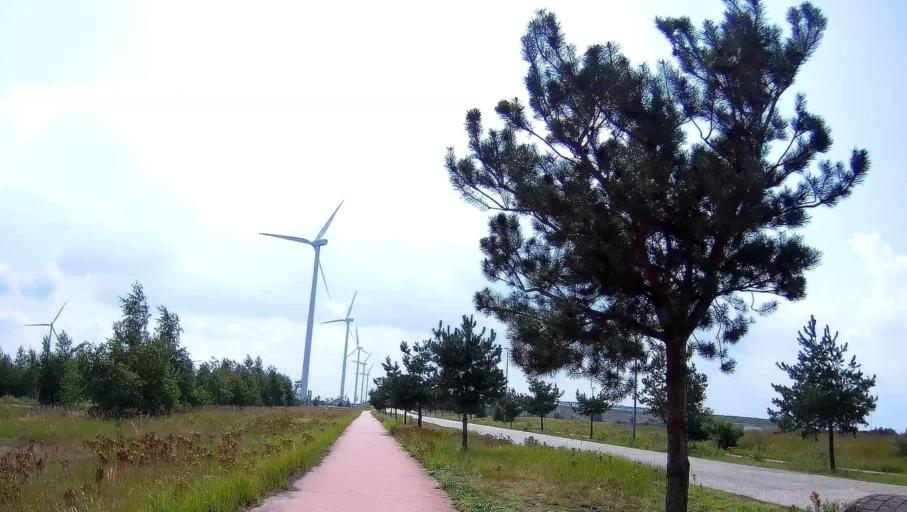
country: BE
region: Flanders
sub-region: Provincie Limburg
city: Lommel
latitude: 51.2091
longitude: 5.2506
